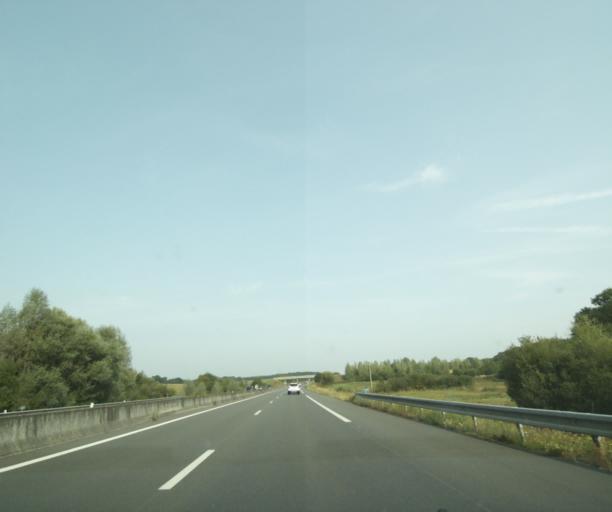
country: FR
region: Pays de la Loire
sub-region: Departement de la Sarthe
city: Champfleur
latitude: 48.3330
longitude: 0.1088
